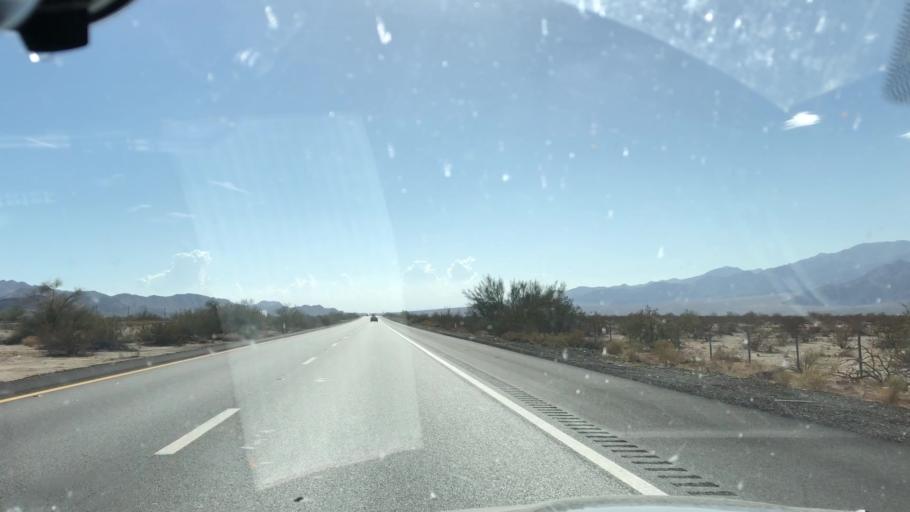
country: US
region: California
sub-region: Imperial County
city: Niland
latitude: 33.6726
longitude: -115.5977
